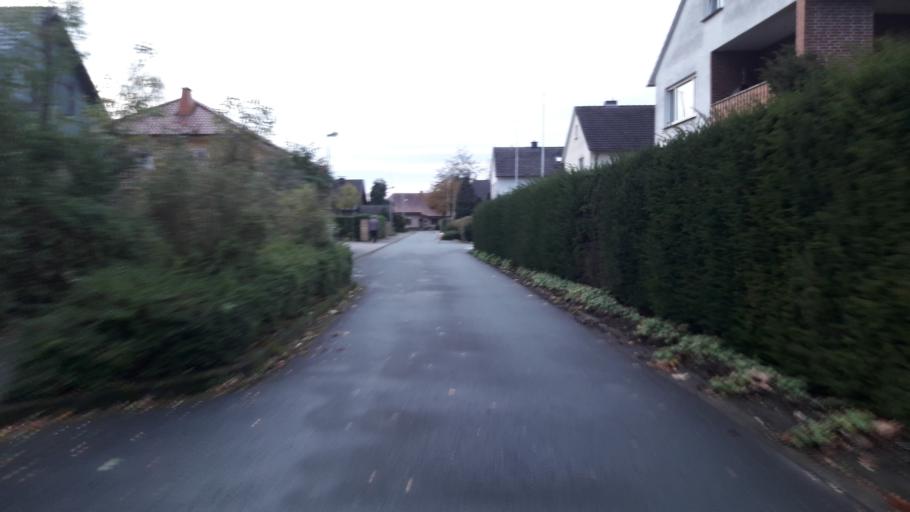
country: DE
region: North Rhine-Westphalia
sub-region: Regierungsbezirk Detmold
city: Delbruck
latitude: 51.7400
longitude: 8.6233
